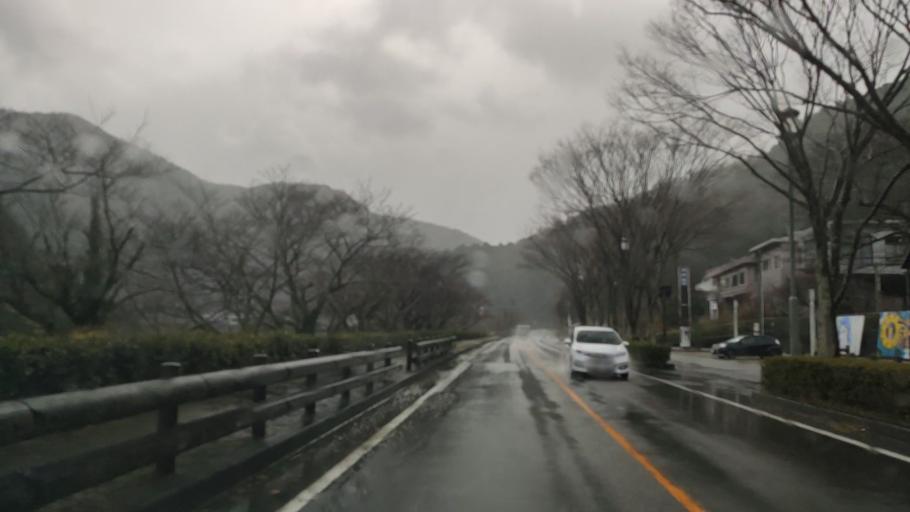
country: JP
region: Tokushima
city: Kamojimacho-jogejima
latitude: 34.1509
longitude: 134.3527
